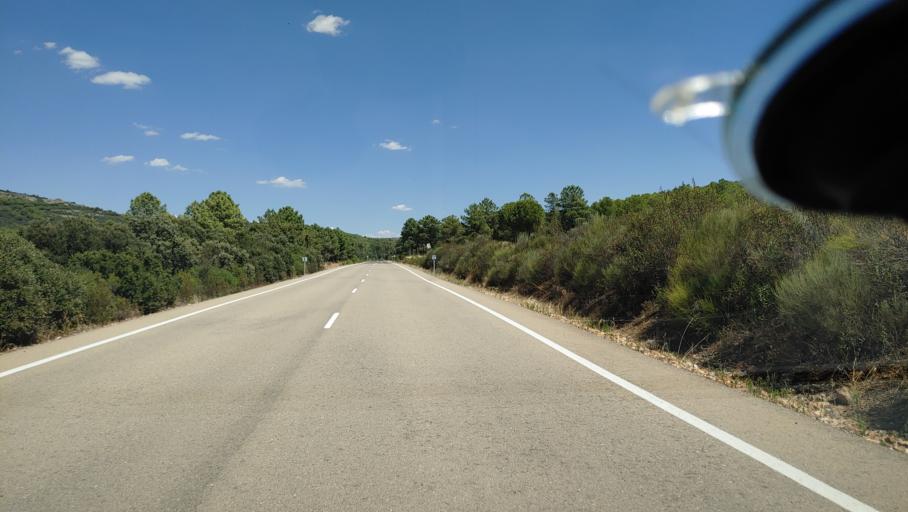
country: ES
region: Castille-La Mancha
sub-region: Provincia de Ciudad Real
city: Saceruela
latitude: 38.9887
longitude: -4.5446
